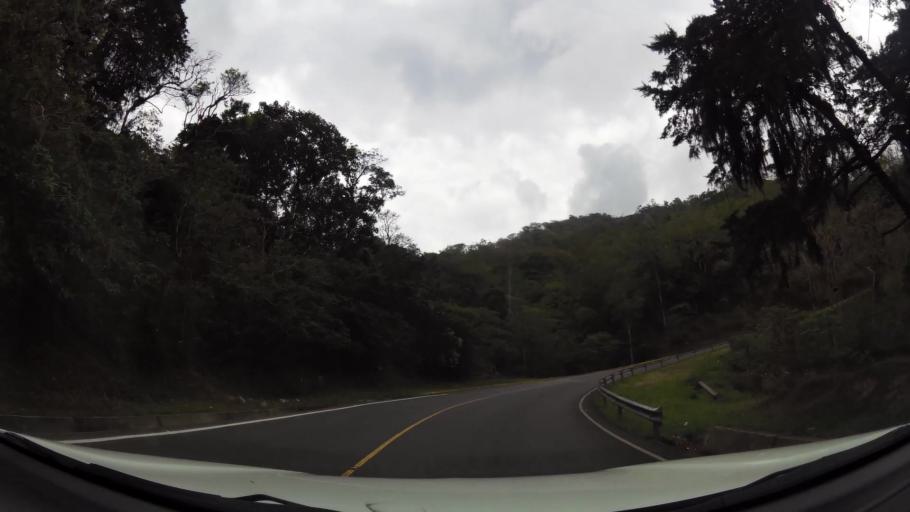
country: NI
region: Matagalpa
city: Matagalpa
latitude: 12.9771
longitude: -85.9225
